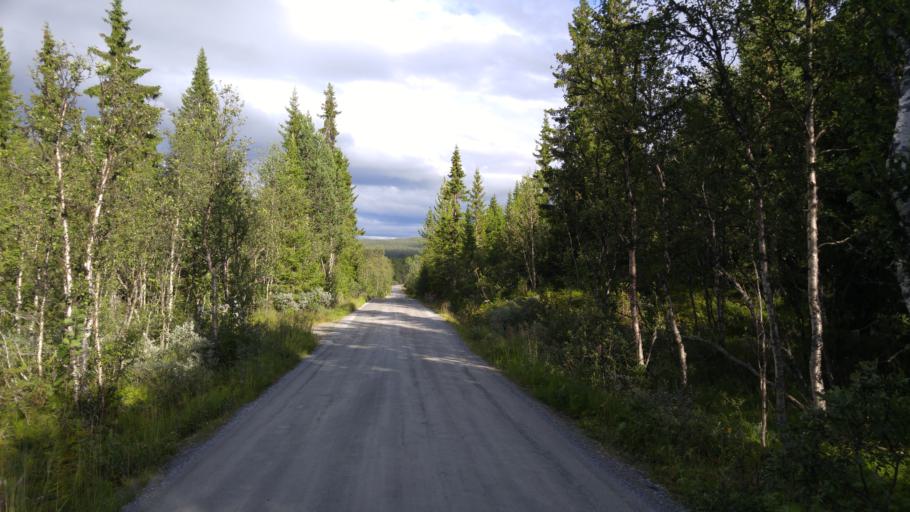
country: NO
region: Buskerud
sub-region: Hemsedal
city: Troim
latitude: 60.8478
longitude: 8.7168
